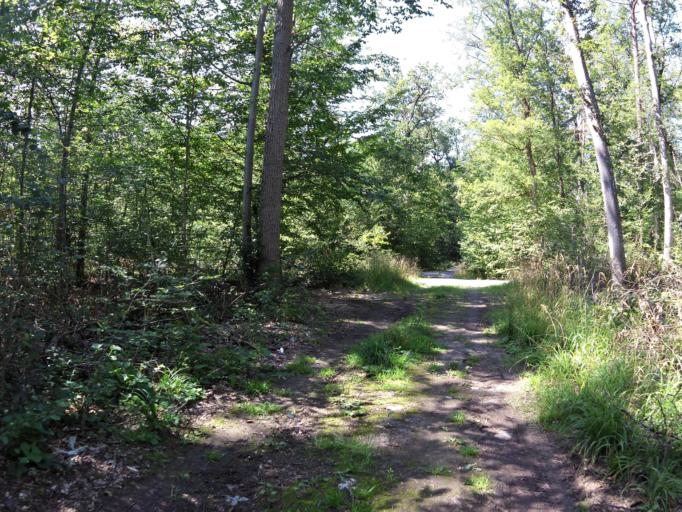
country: DE
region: Bavaria
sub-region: Regierungsbezirk Unterfranken
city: Gadheim
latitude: 49.8555
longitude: 9.8892
